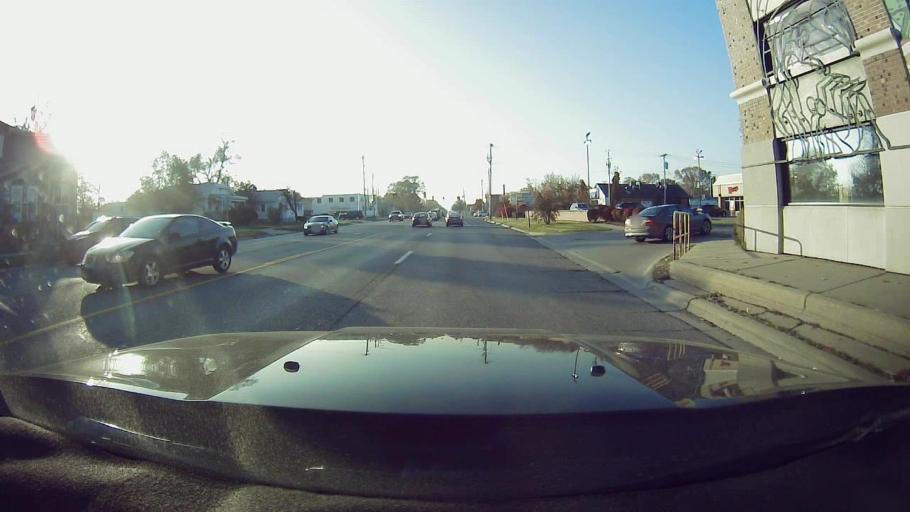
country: US
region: Michigan
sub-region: Oakland County
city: Berkley
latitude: 42.5037
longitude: -83.2033
